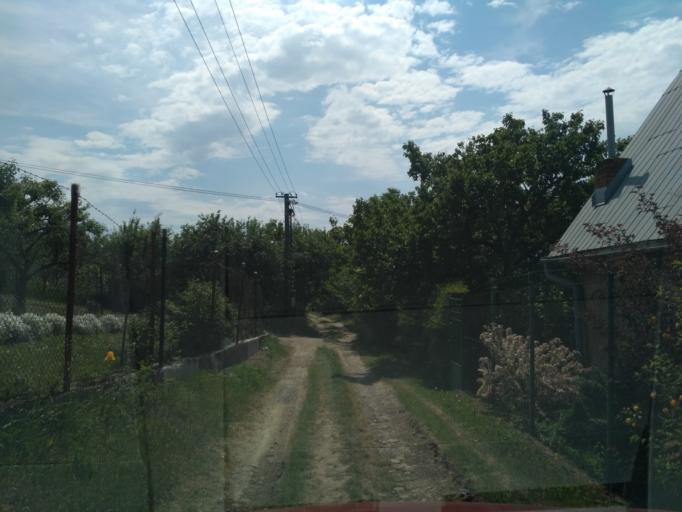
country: SK
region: Kosicky
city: Kosice
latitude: 48.7303
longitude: 21.2227
